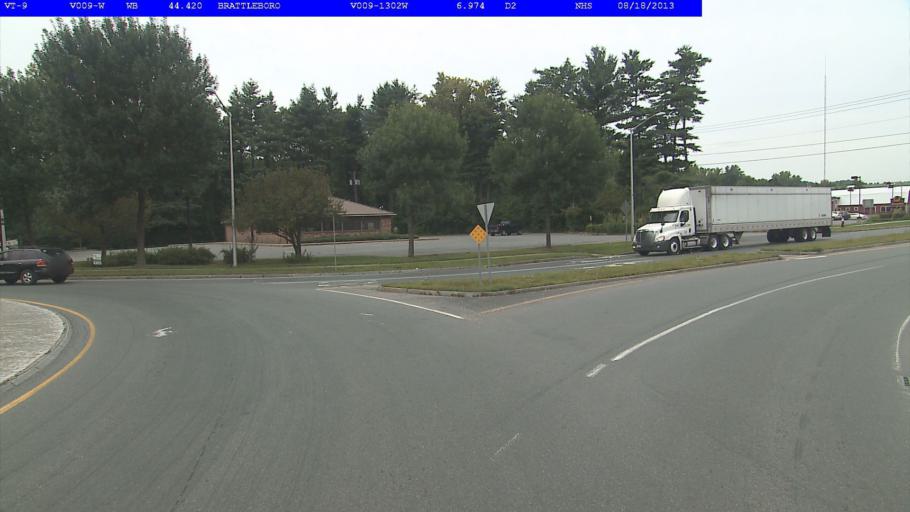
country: US
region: Vermont
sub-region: Windham County
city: Brattleboro
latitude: 42.8850
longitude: -72.5565
